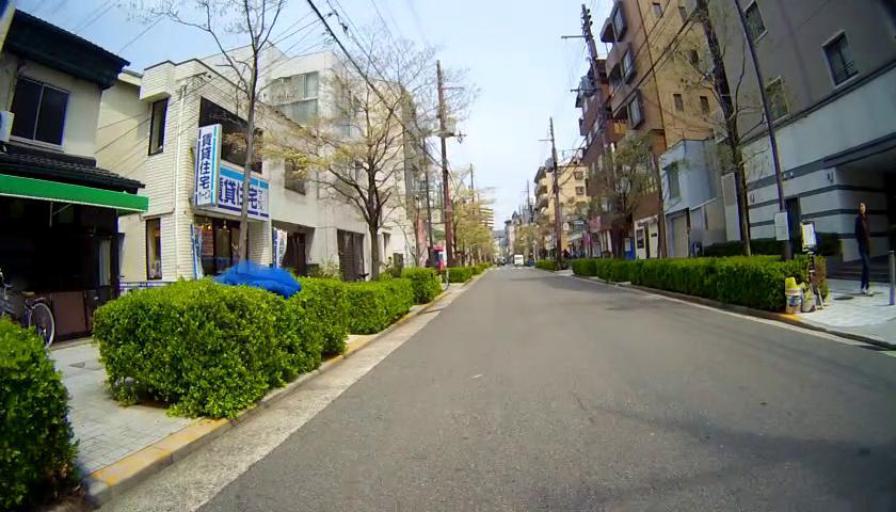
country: JP
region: Osaka
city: Suita
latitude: 34.7487
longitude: 135.5339
